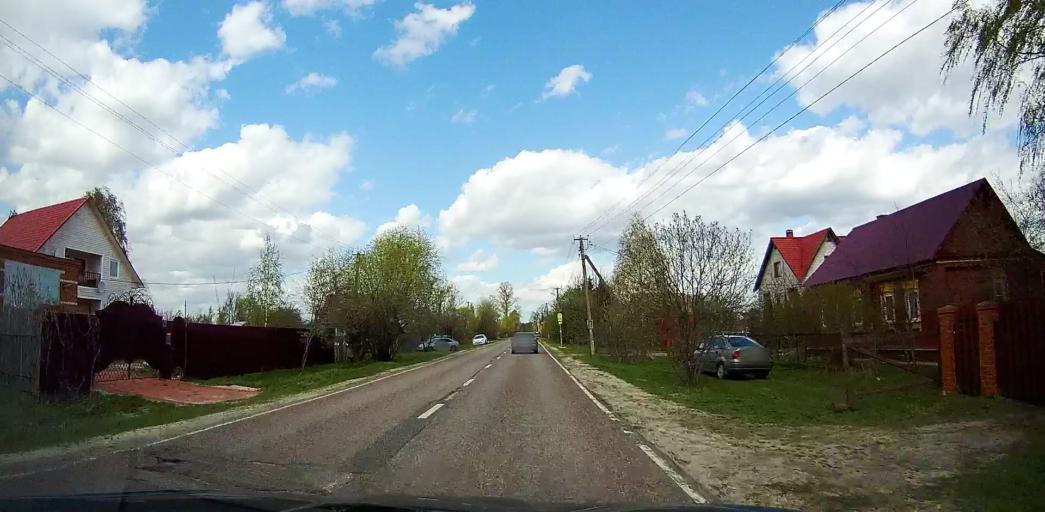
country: RU
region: Moskovskaya
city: Davydovo
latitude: 55.5825
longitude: 38.8260
